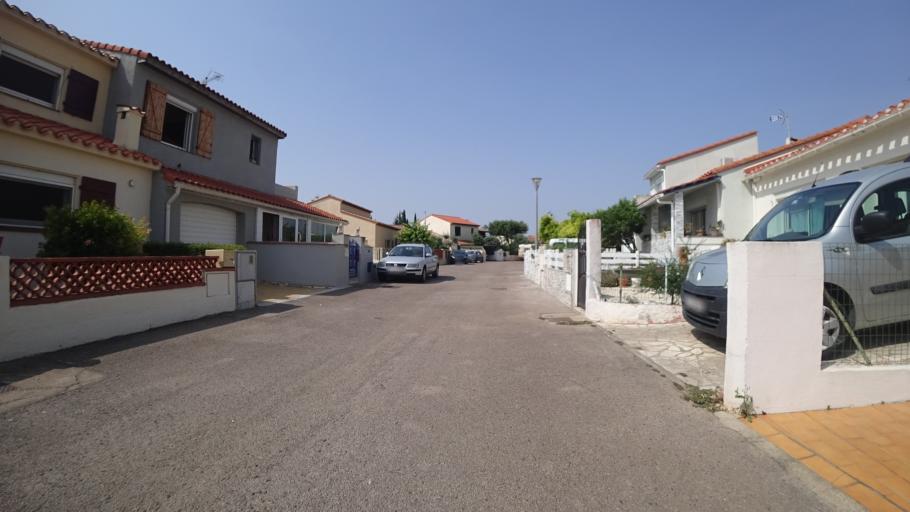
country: FR
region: Languedoc-Roussillon
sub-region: Departement des Pyrenees-Orientales
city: Saint-Laurent-de-la-Salanque
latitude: 42.7708
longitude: 3.0074
